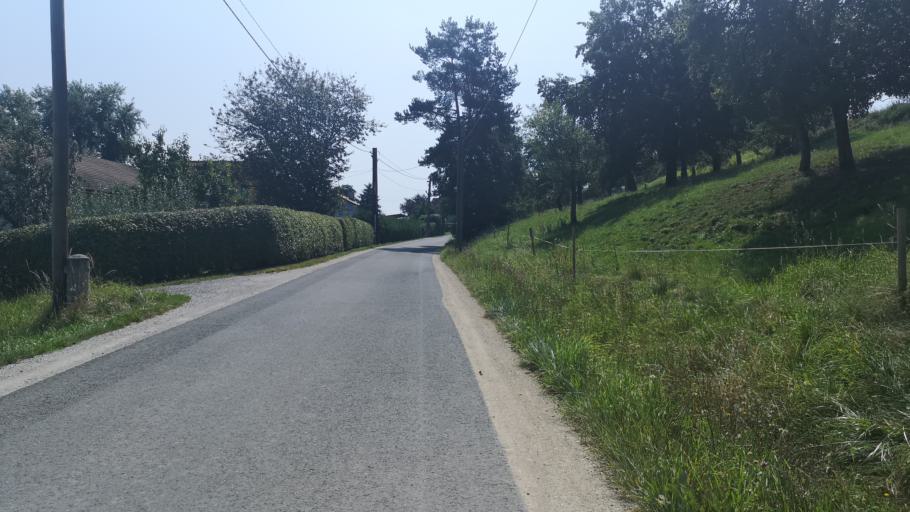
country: AT
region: Styria
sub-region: Politischer Bezirk Deutschlandsberg
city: Lannach
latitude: 46.9347
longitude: 15.3491
